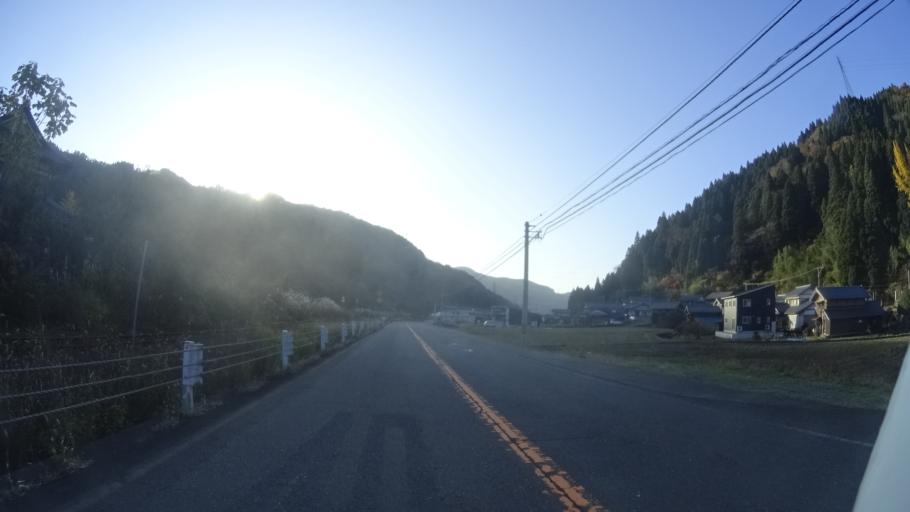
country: JP
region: Fukui
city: Ono
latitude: 35.9975
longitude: 136.4338
